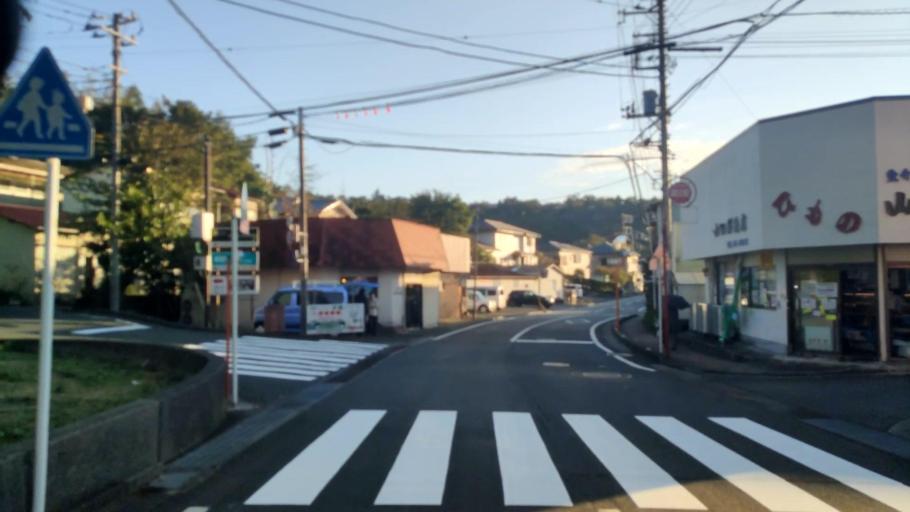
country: JP
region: Shizuoka
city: Ito
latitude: 34.9503
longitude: 139.1234
